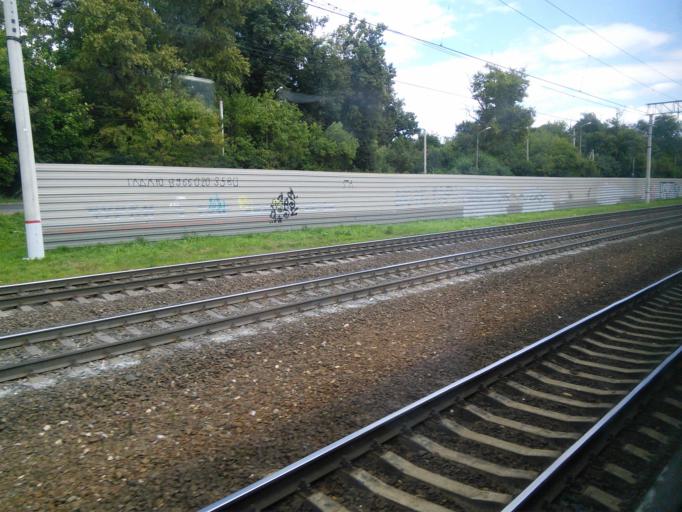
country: RU
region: Moscow
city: Zhulebino
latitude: 55.7026
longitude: 37.8559
